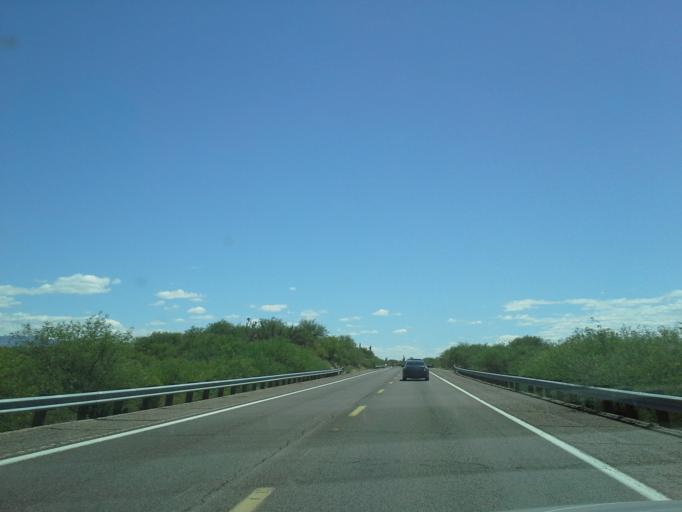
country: US
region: Arizona
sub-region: Pinal County
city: Mammoth
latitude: 32.8243
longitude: -110.6965
